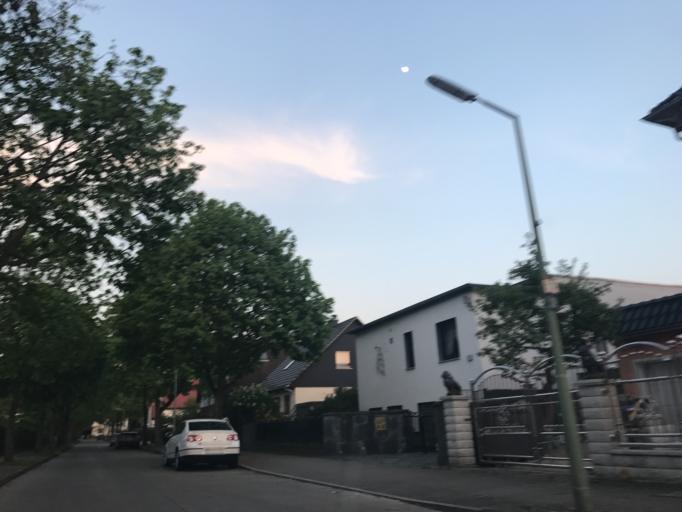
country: DE
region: Berlin
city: Wilhelmstadt
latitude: 52.5191
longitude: 13.1606
